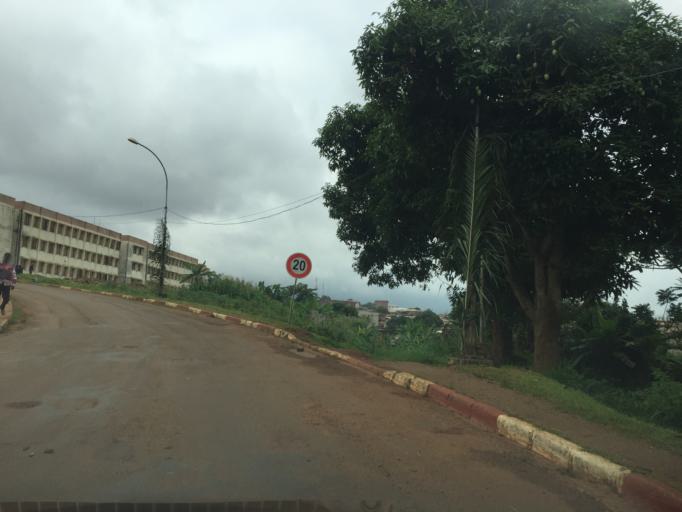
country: CM
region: Centre
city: Yaounde
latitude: 3.8601
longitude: 11.4963
